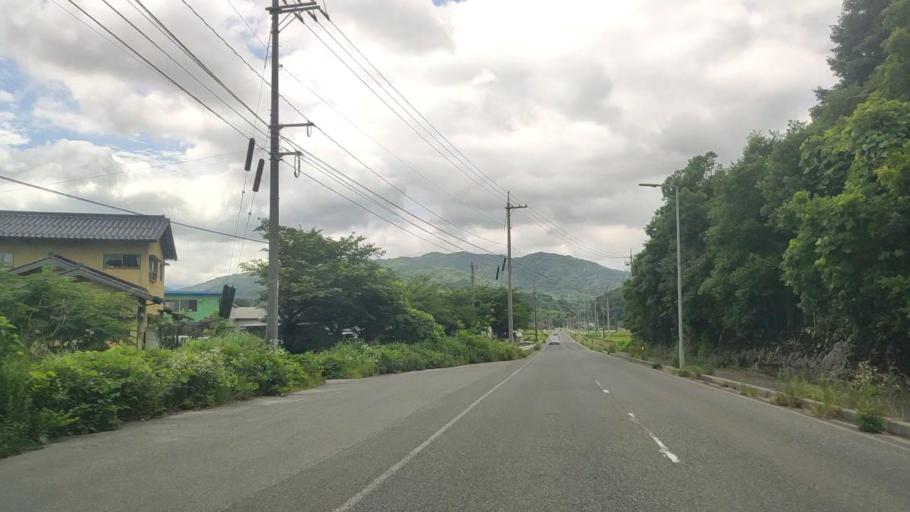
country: JP
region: Tottori
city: Yonago
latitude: 35.3354
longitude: 133.4341
